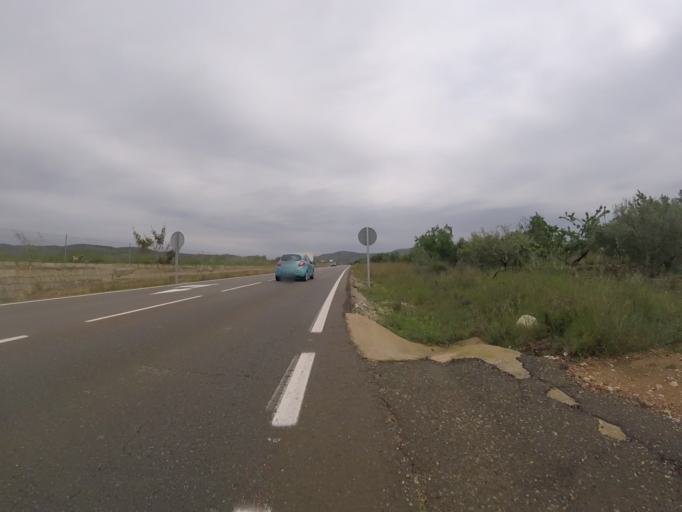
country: ES
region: Valencia
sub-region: Provincia de Castello
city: Alcoceber
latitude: 40.2576
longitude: 0.2444
